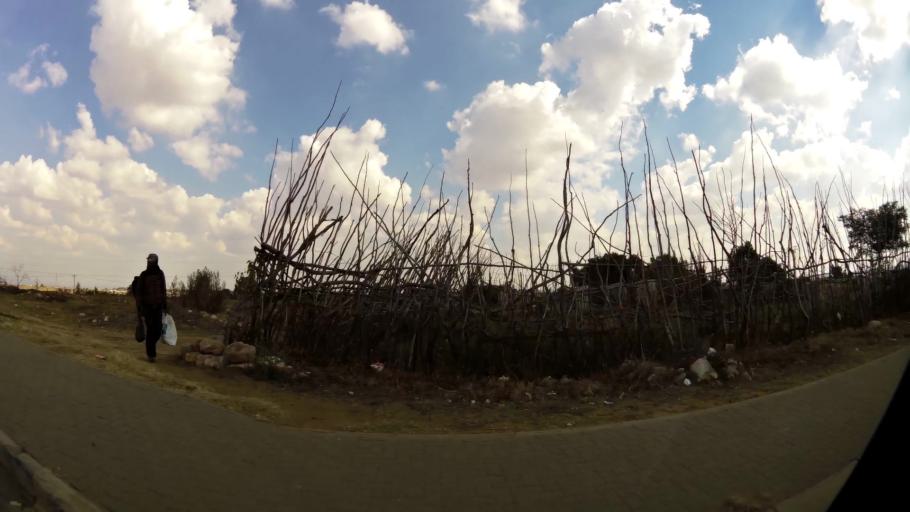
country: ZA
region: Gauteng
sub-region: City of Johannesburg Metropolitan Municipality
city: Roodepoort
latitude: -26.1849
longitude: 27.8552
